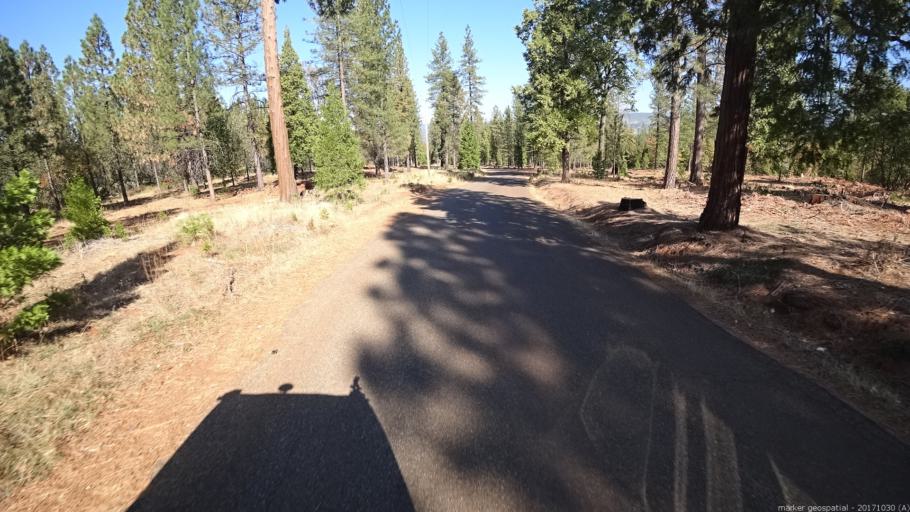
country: US
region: California
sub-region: Shasta County
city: Shingletown
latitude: 40.6248
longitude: -121.8955
